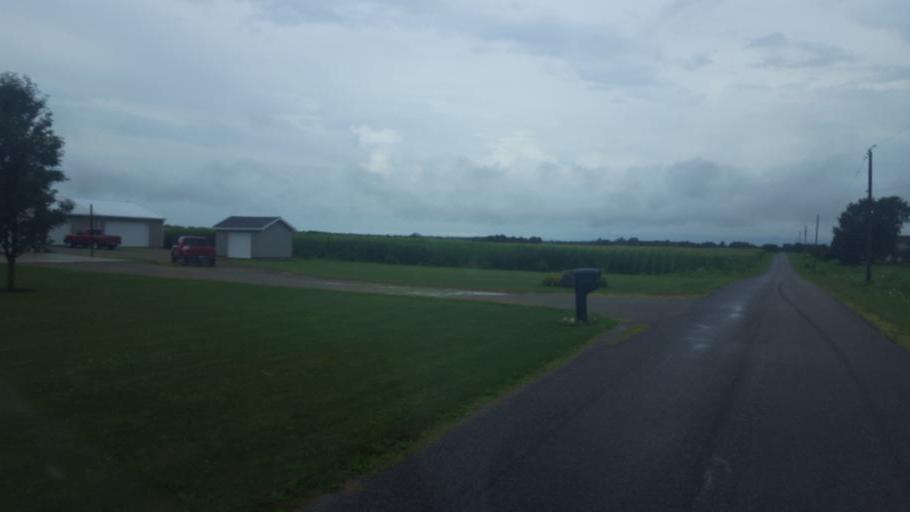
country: US
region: Ohio
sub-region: Union County
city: Richwood
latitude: 40.4964
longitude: -83.2985
